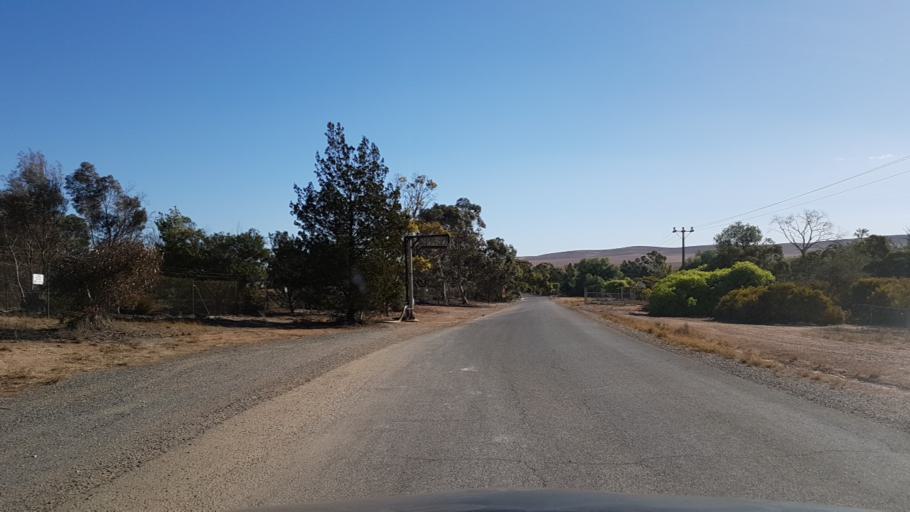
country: AU
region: South Australia
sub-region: Clare and Gilbert Valleys
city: Clare
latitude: -33.6754
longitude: 138.9202
